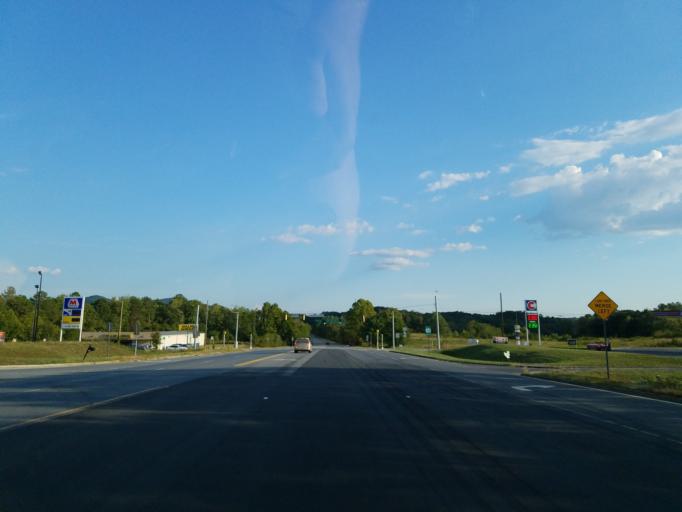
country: US
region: Georgia
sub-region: Murray County
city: Chatsworth
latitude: 34.6977
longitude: -84.7387
